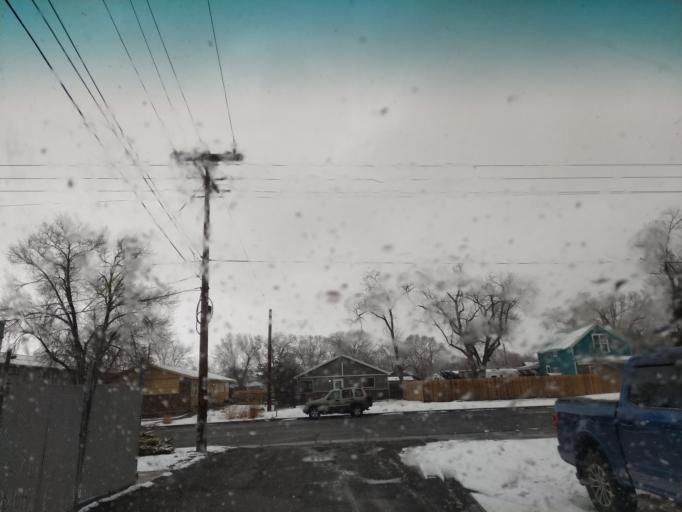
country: US
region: Colorado
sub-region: Montrose County
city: Montrose
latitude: 38.4851
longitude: -107.8834
